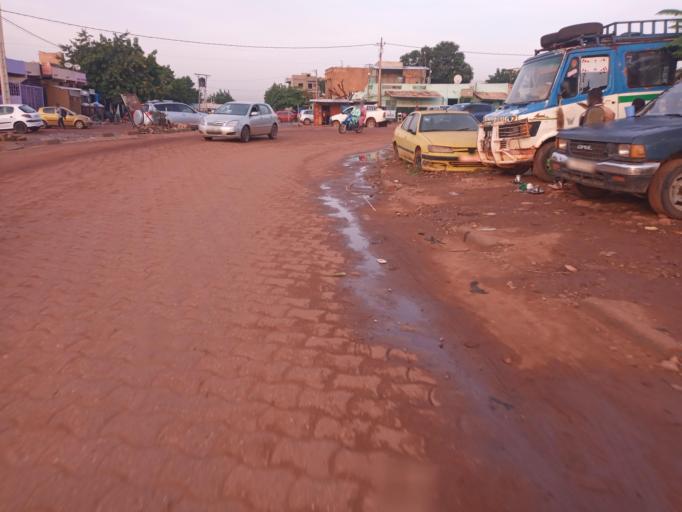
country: ML
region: Bamako
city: Bamako
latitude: 12.6441
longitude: -8.0316
